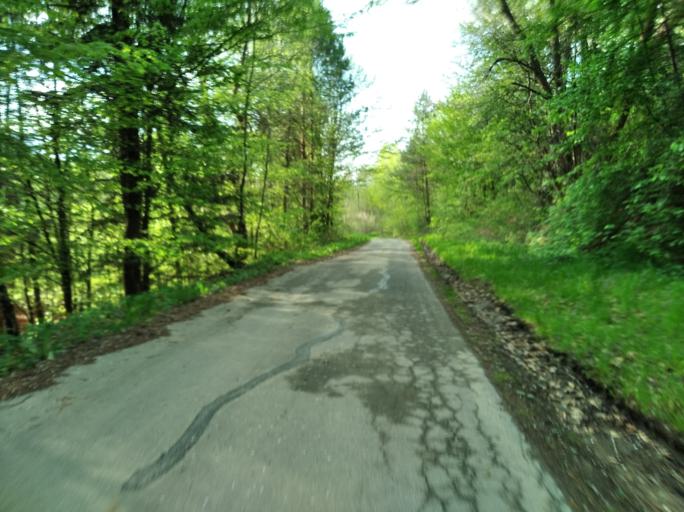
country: PL
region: Subcarpathian Voivodeship
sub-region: Powiat strzyzowski
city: Wysoka Strzyzowska
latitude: 49.7999
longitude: 21.7554
